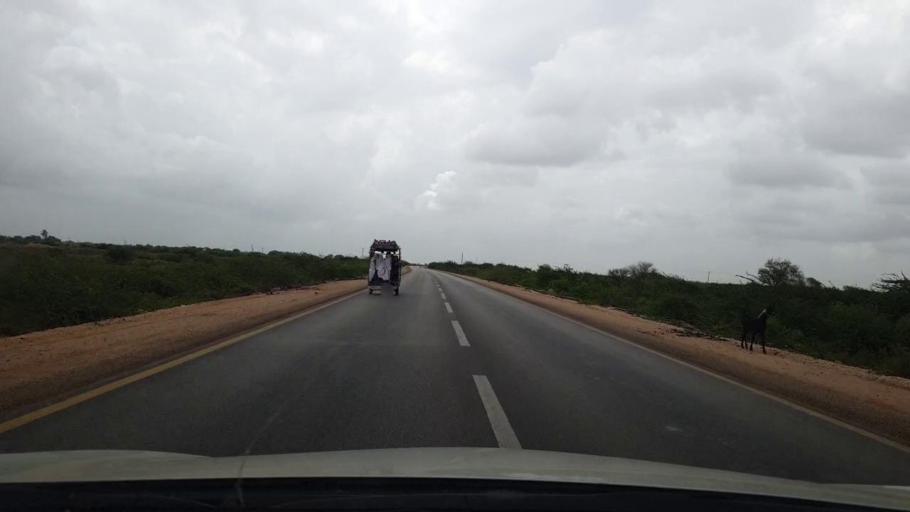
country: PK
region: Sindh
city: Mirpur Batoro
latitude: 24.6323
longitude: 68.3708
